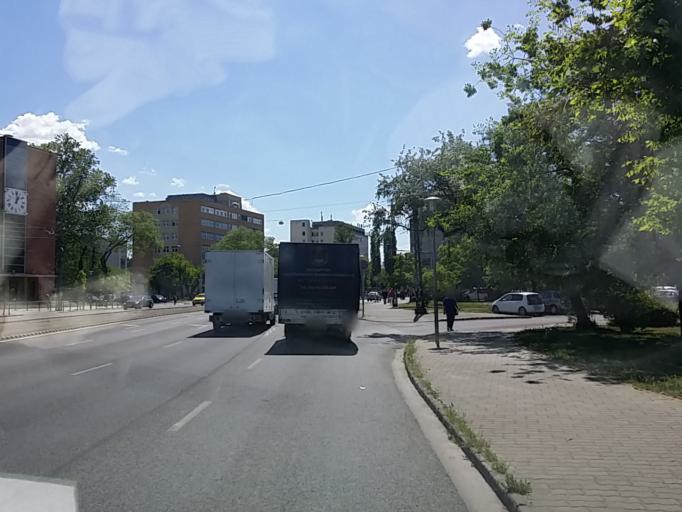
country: HU
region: Budapest
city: Budapest XIII. keruelet
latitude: 47.5309
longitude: 19.0804
